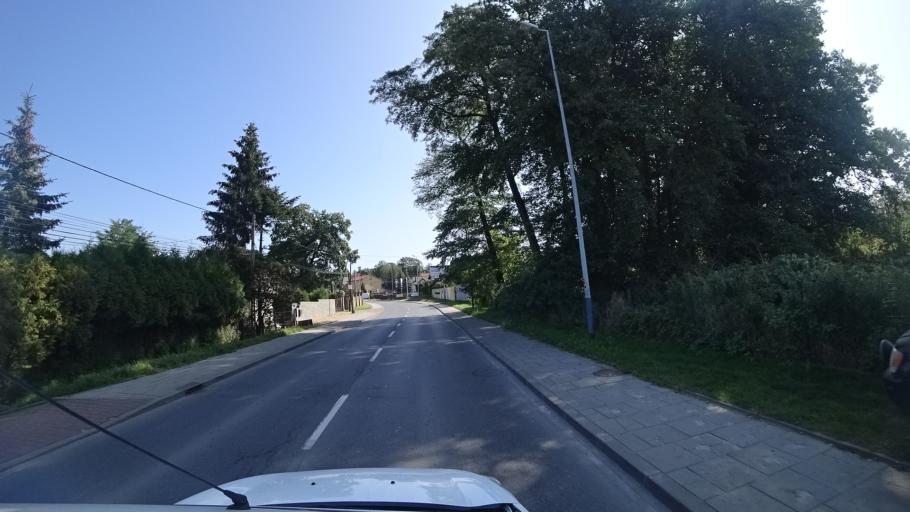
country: PL
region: Lesser Poland Voivodeship
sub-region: Powiat krakowski
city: Libertow
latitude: 50.0076
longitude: 19.9172
